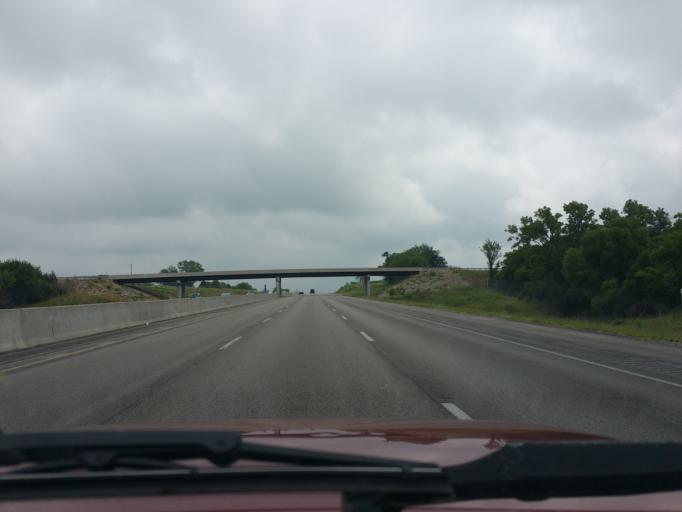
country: US
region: Kansas
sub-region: Shawnee County
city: Topeka
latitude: 39.0140
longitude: -95.4757
